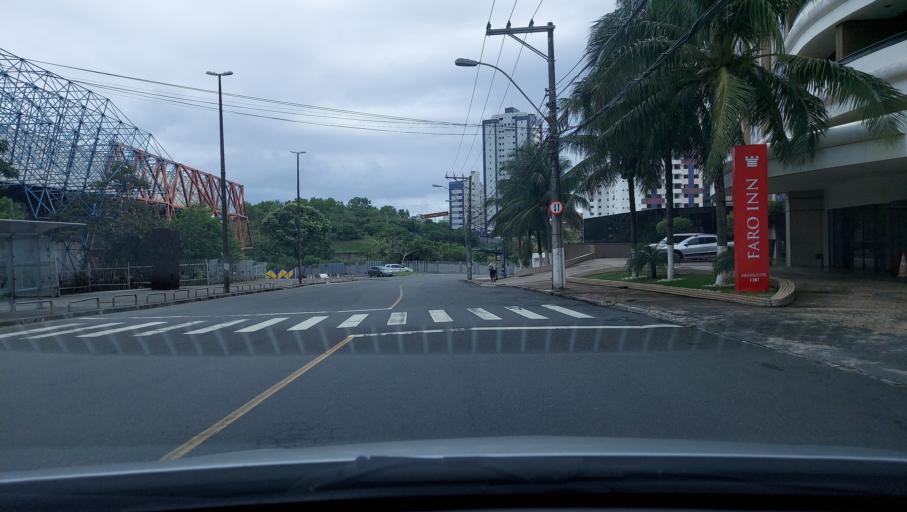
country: BR
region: Bahia
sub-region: Salvador
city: Salvador
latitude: -12.9820
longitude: -38.4412
